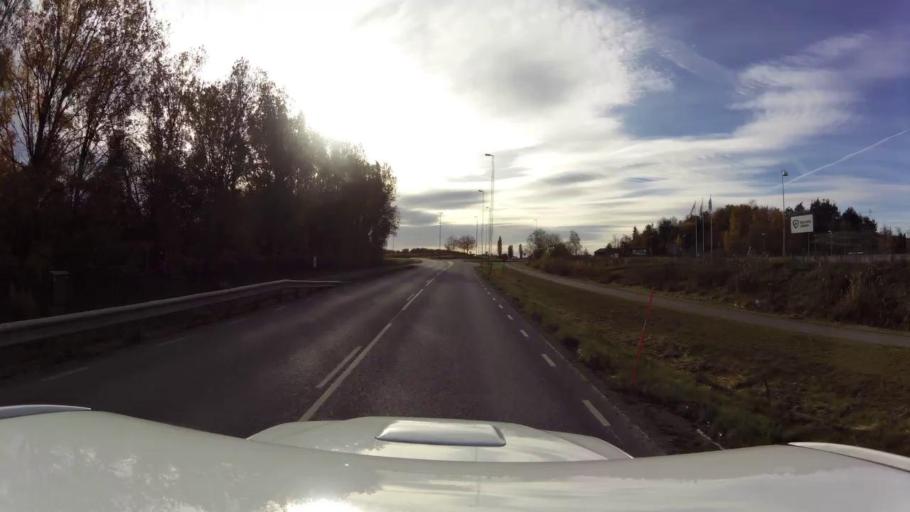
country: SE
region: OEstergoetland
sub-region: Linkopings Kommun
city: Ekangen
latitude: 58.4351
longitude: 15.6462
